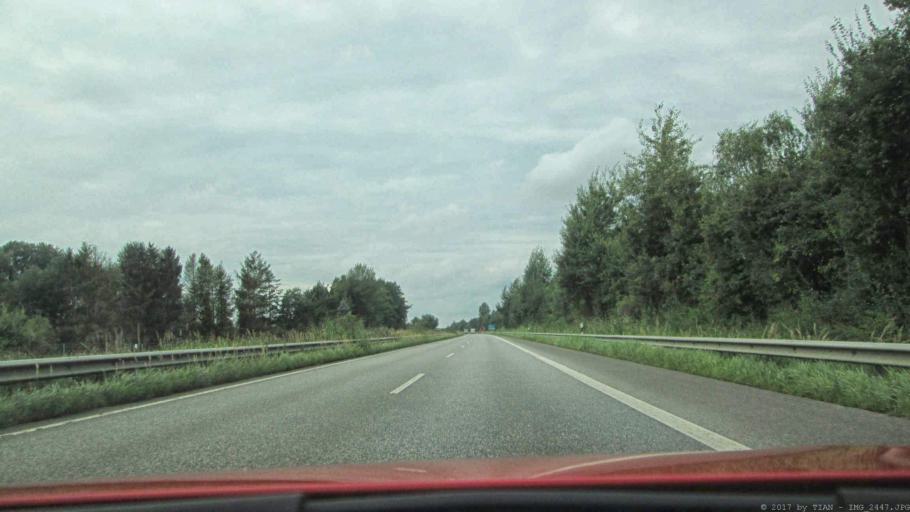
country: DE
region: Schleswig-Holstein
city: Bornsen
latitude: 53.4646
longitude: 10.2769
